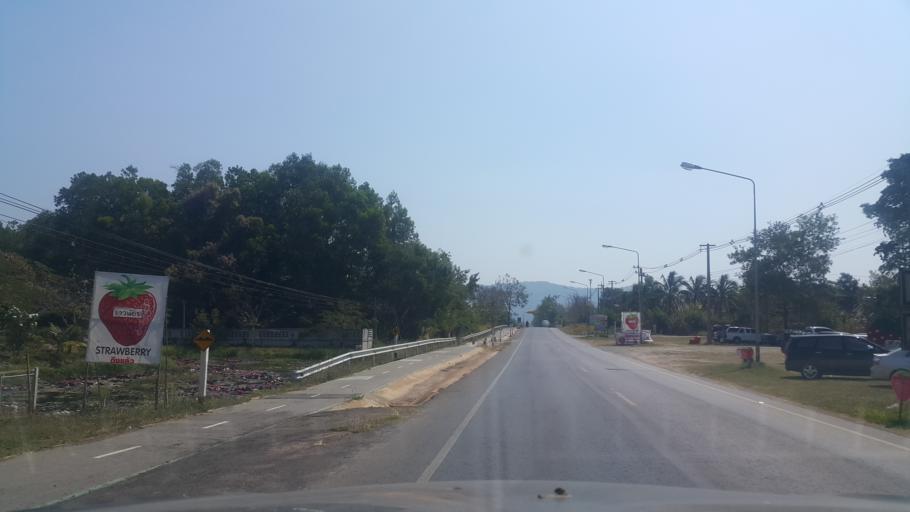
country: TH
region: Nakhon Ratchasima
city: Wang Nam Khiao
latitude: 14.3641
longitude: 101.9114
